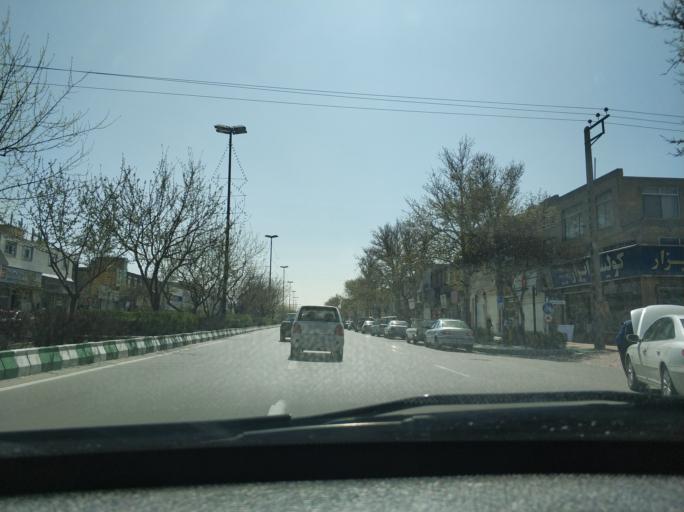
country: IR
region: Razavi Khorasan
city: Mashhad
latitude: 36.2646
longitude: 59.6020
